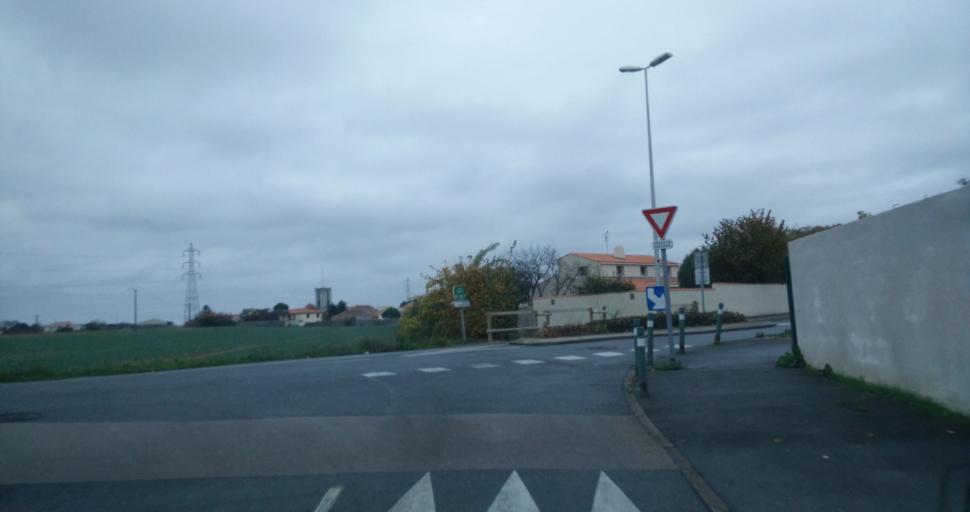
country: FR
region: Poitou-Charentes
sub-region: Departement de la Charente-Maritime
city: Puilboreau
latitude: 46.1884
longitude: -1.1219
